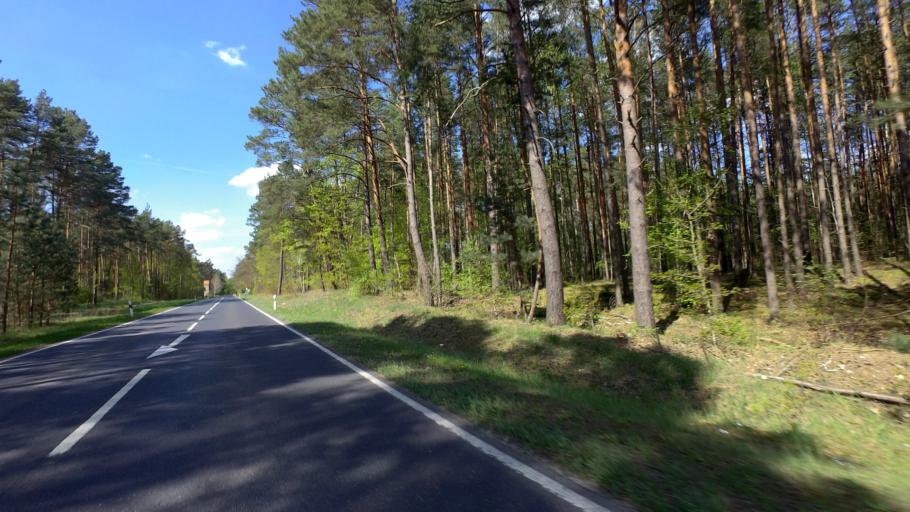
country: DE
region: Brandenburg
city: Templin
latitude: 53.1228
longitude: 13.5412
